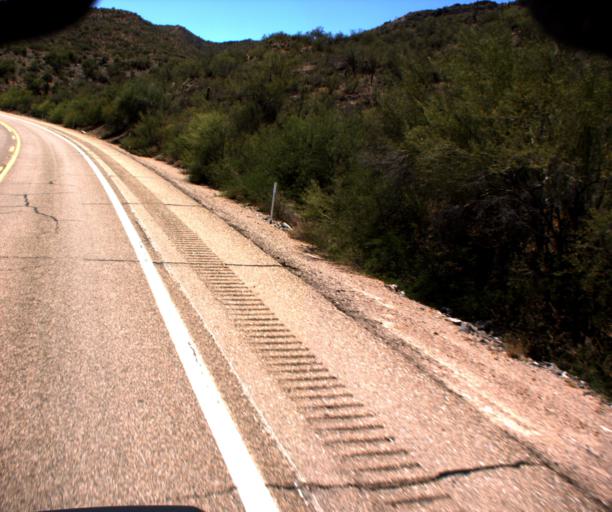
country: US
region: Arizona
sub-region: Pinal County
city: Kearny
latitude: 33.0389
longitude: -110.7292
